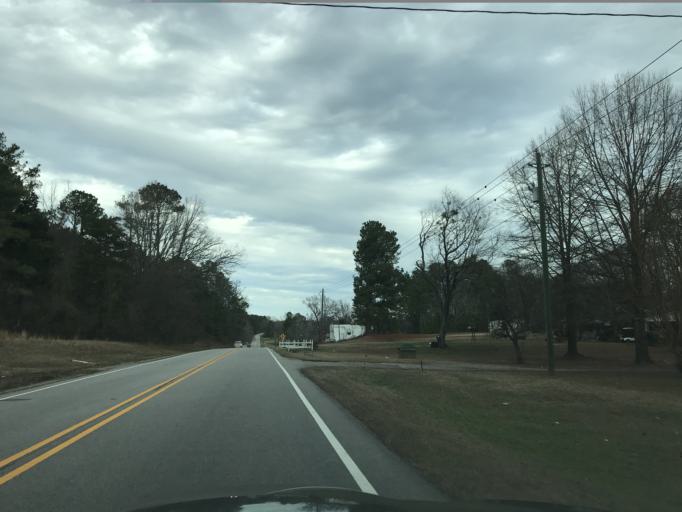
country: US
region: North Carolina
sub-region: Franklin County
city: Louisburg
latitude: 36.0244
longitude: -78.3544
